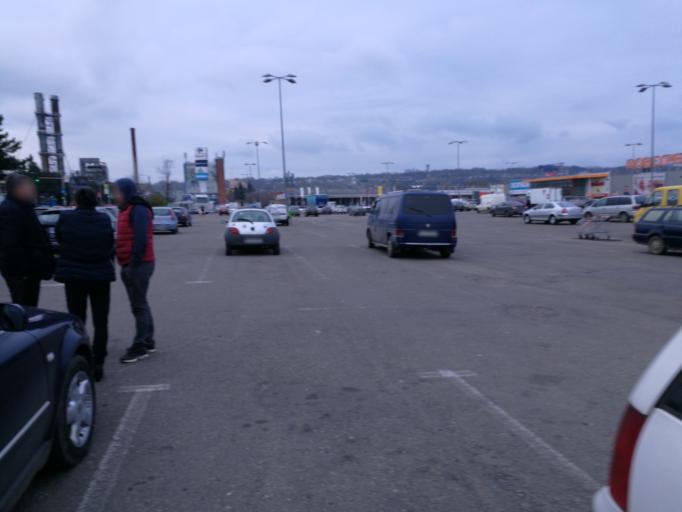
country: RO
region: Suceava
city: Suceava
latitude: 47.6647
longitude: 26.2691
